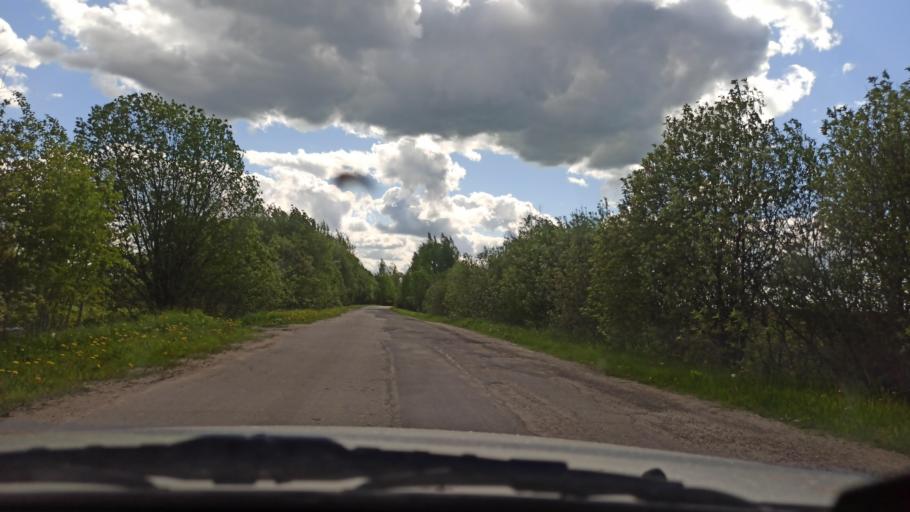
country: RU
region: Vologda
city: Molochnoye
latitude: 59.3738
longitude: 39.7063
